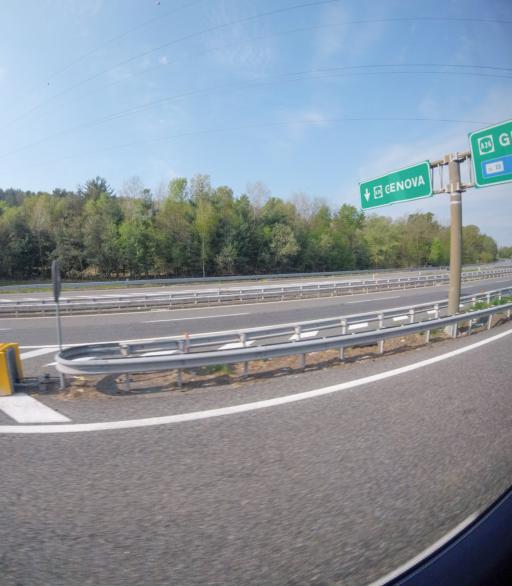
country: IT
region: Piedmont
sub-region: Provincia di Novara
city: Comignago
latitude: 45.7085
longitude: 8.5616
